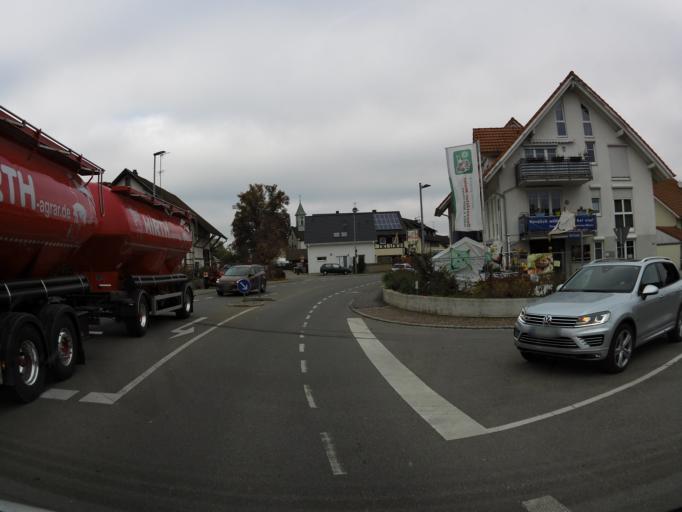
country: DE
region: Baden-Wuerttemberg
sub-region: Freiburg Region
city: Moos
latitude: 47.7241
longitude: 8.9347
